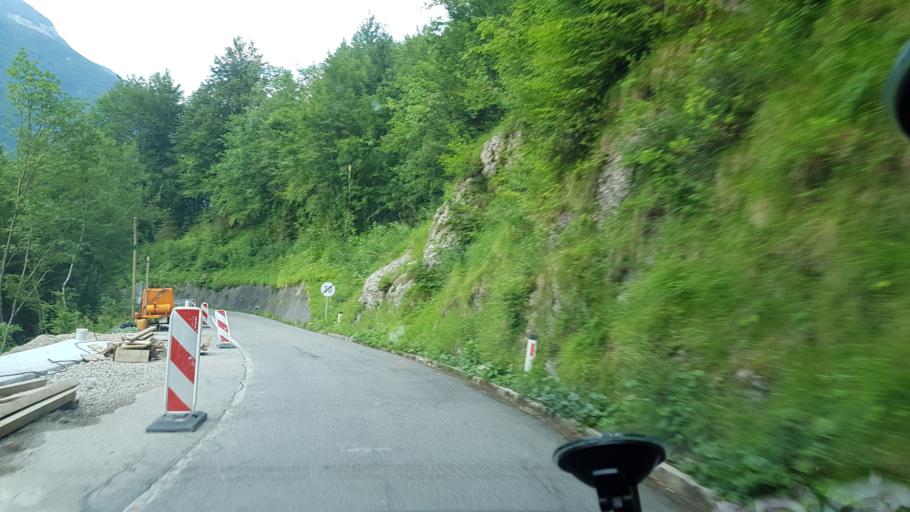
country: SI
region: Bovec
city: Bovec
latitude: 46.3017
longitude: 13.4538
